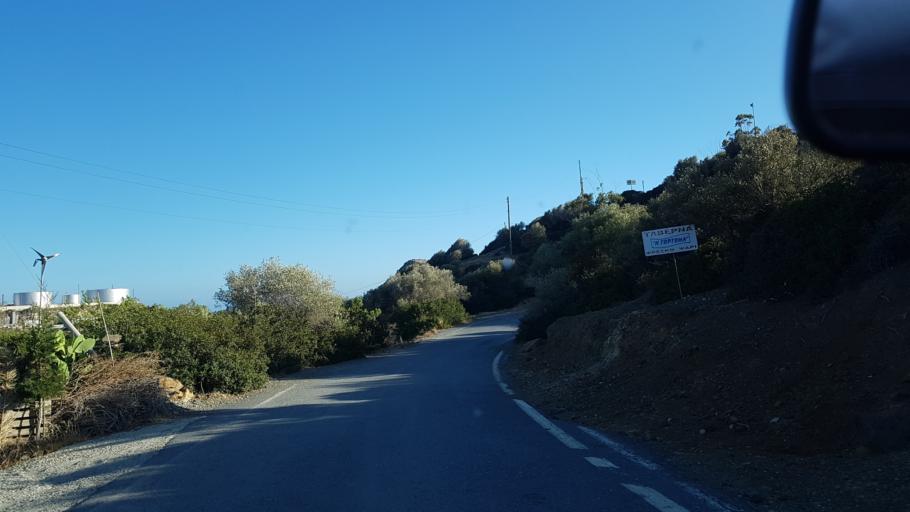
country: GR
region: Crete
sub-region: Nomos Irakleiou
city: Moires
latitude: 34.9344
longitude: 24.8048
